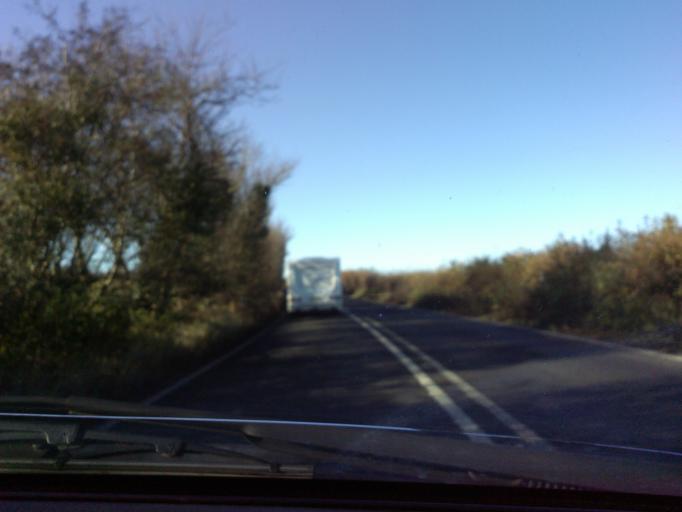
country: GB
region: England
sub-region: Dorset
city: Lytchett Matravers
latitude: 50.7875
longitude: -2.0782
